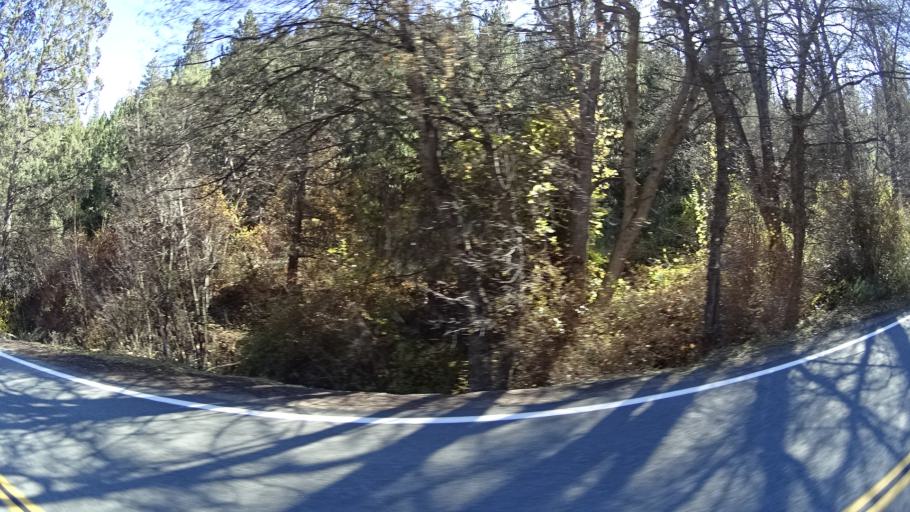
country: US
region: California
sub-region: Siskiyou County
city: Weed
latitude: 41.4595
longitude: -122.6245
